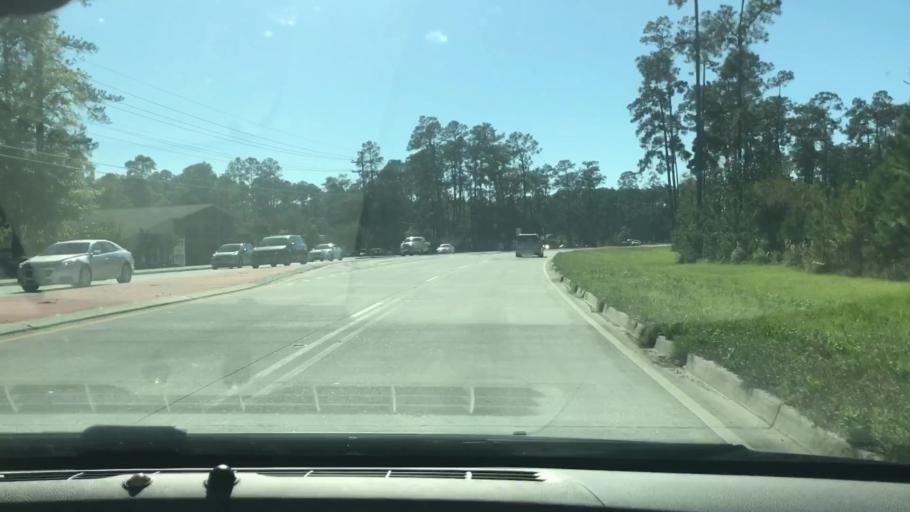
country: US
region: Louisiana
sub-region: Saint Tammany Parish
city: Covington
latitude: 30.4608
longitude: -90.1205
